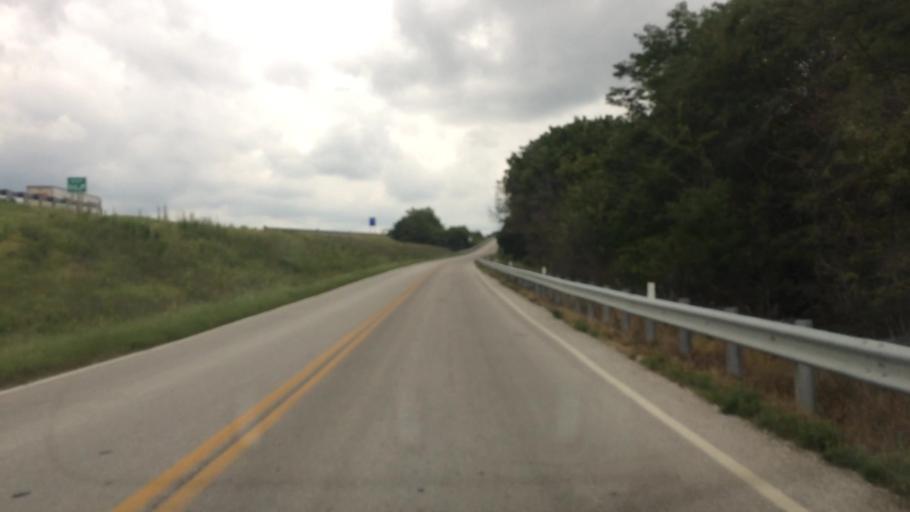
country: US
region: Missouri
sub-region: Webster County
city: Marshfield
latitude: 37.3032
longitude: -92.9948
